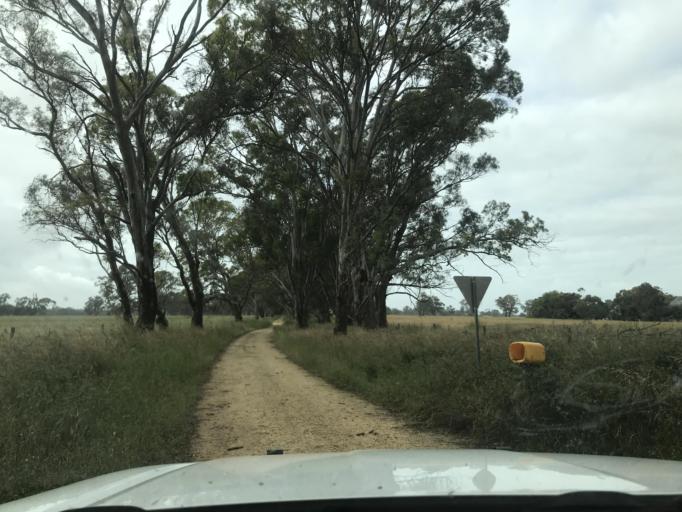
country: AU
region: South Australia
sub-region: Naracoorte and Lucindale
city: Naracoorte
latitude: -37.0925
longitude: 141.0763
